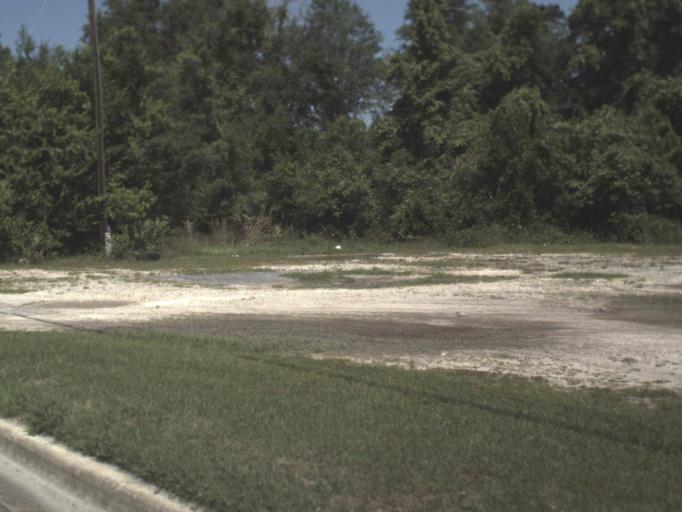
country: US
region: Florida
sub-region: Columbia County
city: Watertown
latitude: 30.1865
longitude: -82.5979
